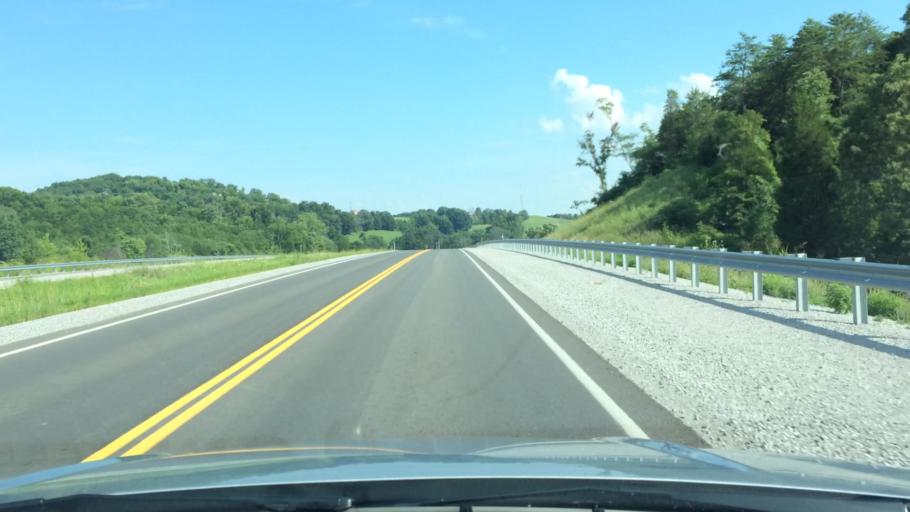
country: US
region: Tennessee
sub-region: Jefferson County
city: White Pine
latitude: 36.1370
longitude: -83.3400
